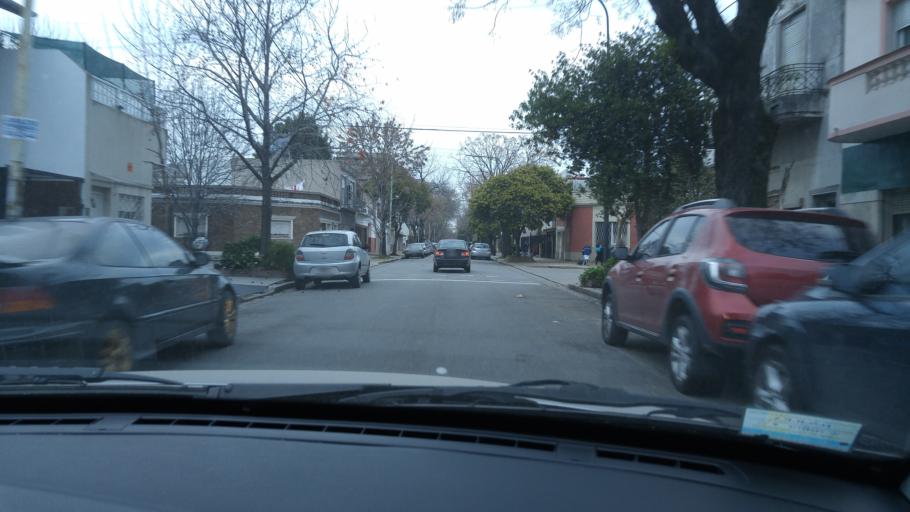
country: AR
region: Buenos Aires
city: Caseros
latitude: -34.6256
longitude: -58.5251
